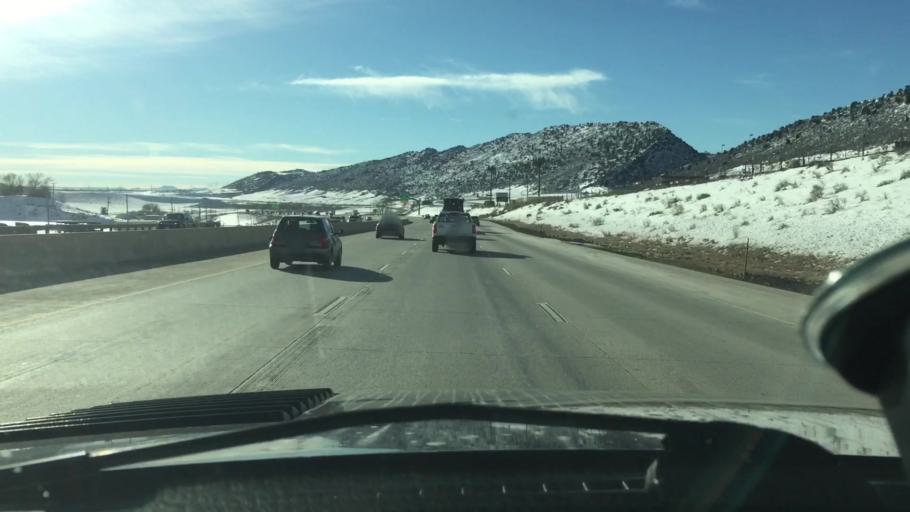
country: US
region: Colorado
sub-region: Jefferson County
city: West Pleasant View
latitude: 39.6666
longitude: -105.1868
